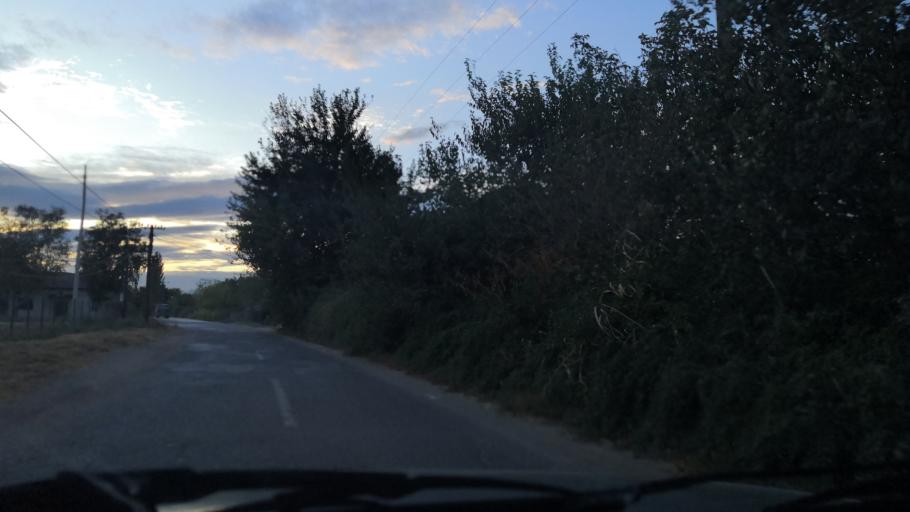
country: RO
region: Mehedinti
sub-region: Comuna Gogosu
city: Balta Verde
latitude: 44.2900
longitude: 22.6087
